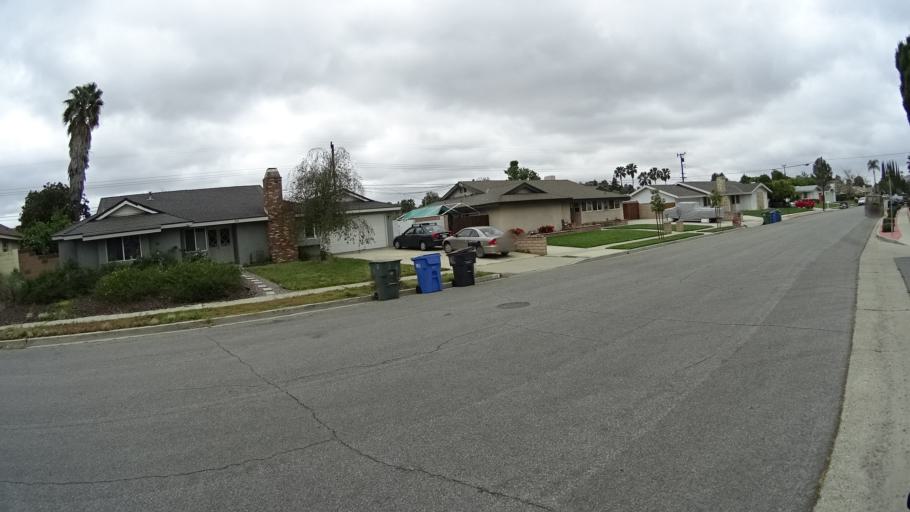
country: US
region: California
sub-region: Ventura County
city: Thousand Oaks
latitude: 34.2074
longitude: -118.8748
